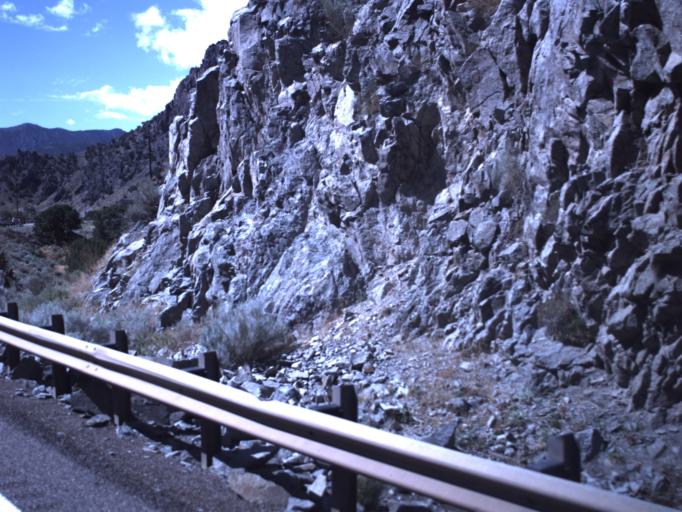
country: US
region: Utah
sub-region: Sevier County
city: Monroe
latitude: 38.5498
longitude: -112.2685
